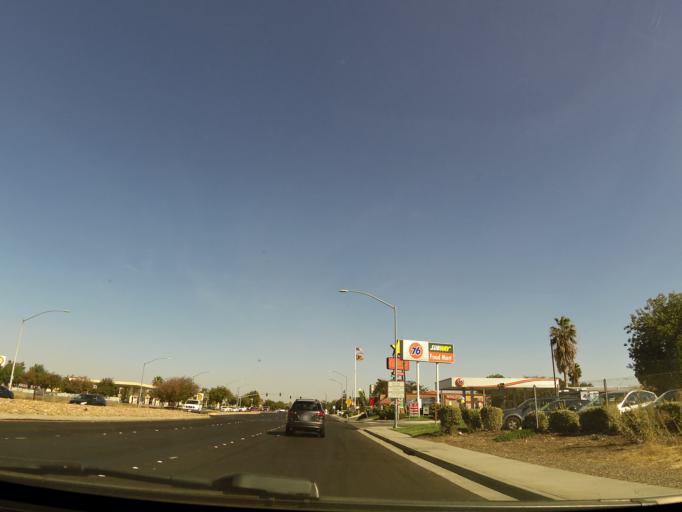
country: US
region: California
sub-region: San Joaquin County
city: Tracy
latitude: 37.7540
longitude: -121.4616
